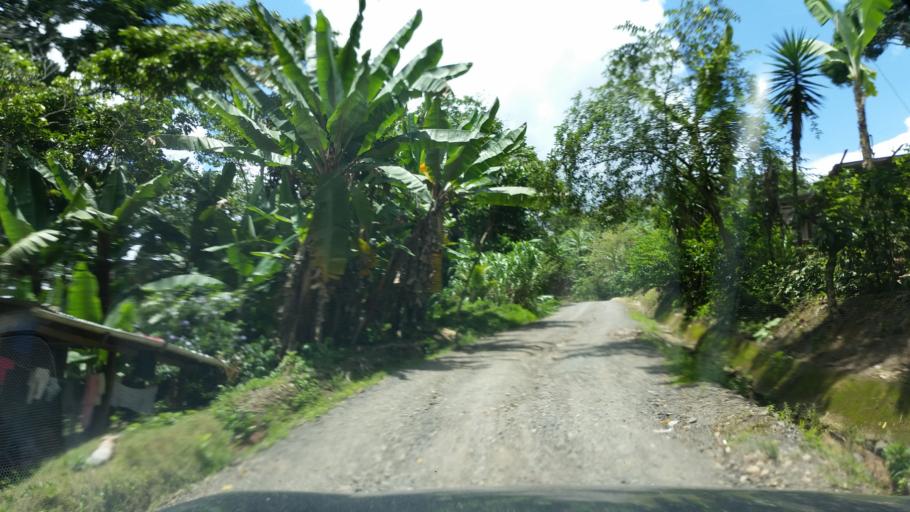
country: NI
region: Atlantico Norte (RAAN)
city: Waslala
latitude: 13.2519
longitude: -85.6167
